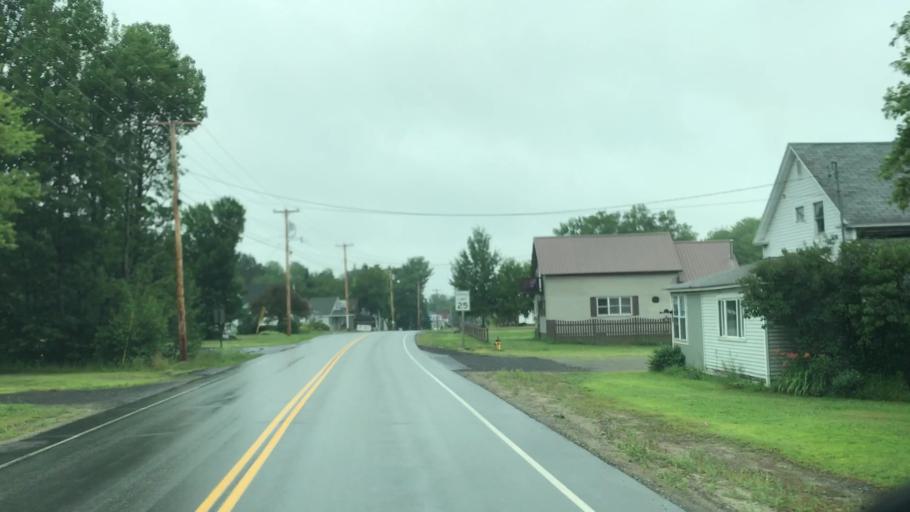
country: US
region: Maine
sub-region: Penobscot County
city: Howland
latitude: 45.2379
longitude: -68.6680
